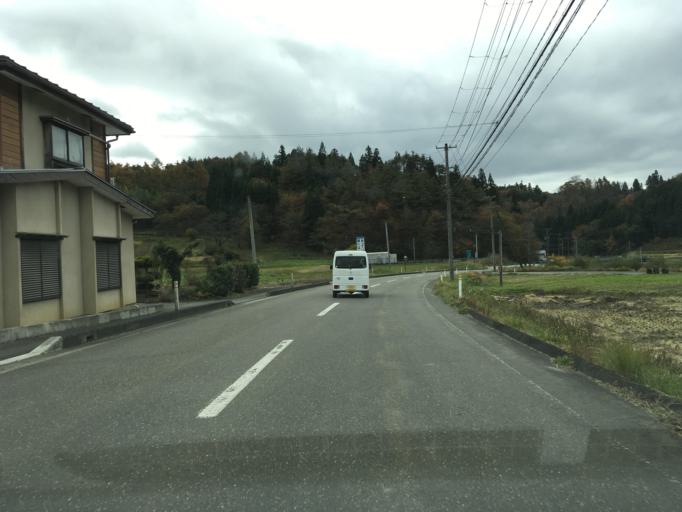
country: JP
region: Iwate
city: Mizusawa
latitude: 39.0607
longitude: 141.3618
